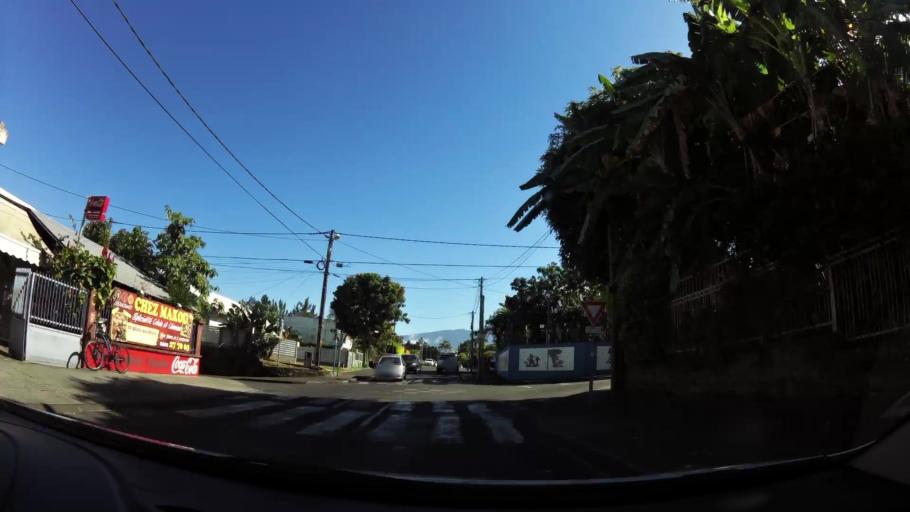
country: RE
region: Reunion
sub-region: Reunion
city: Le Tampon
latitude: -21.2792
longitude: 55.5196
